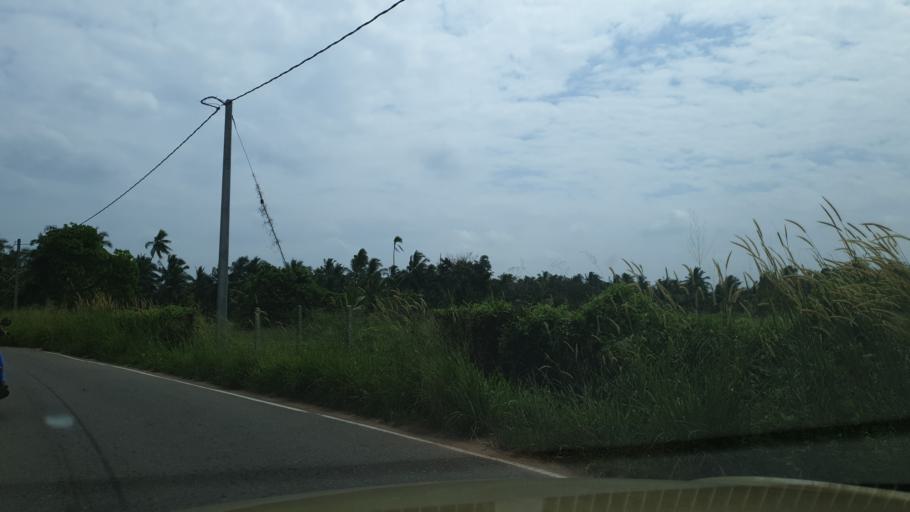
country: LK
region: North Western
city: Kuliyapitiya
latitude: 7.3538
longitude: 79.9676
